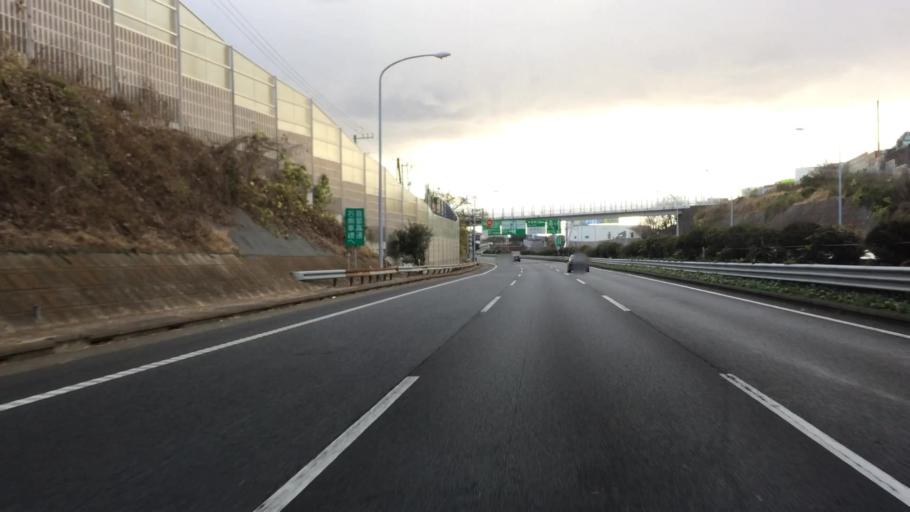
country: JP
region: Kanagawa
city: Yokohama
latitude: 35.4902
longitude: 139.5924
